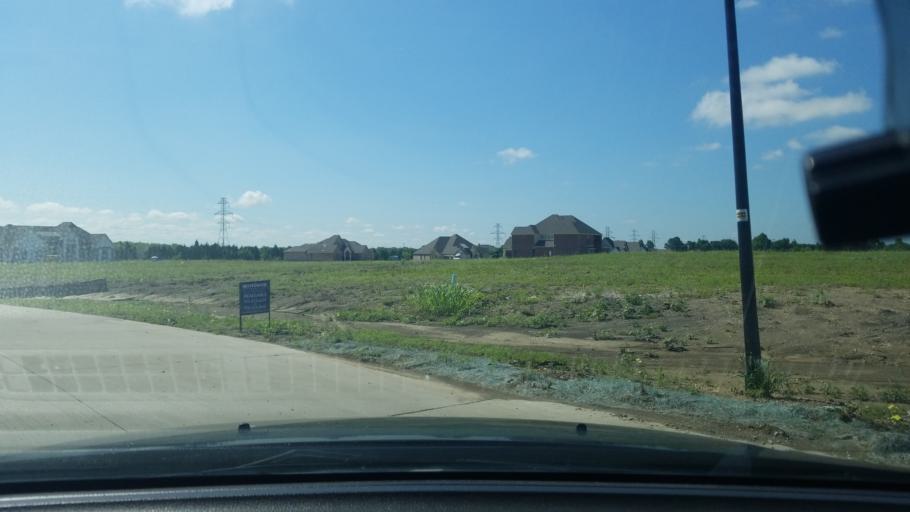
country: US
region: Texas
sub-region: Dallas County
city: Sunnyvale
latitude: 32.8016
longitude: -96.5757
